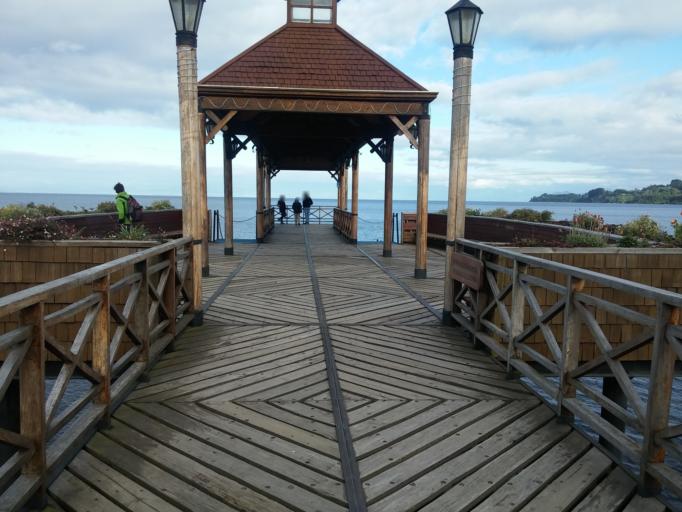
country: CL
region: Los Lagos
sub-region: Provincia de Llanquihue
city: Frutillar
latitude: -41.1359
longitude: -73.0268
